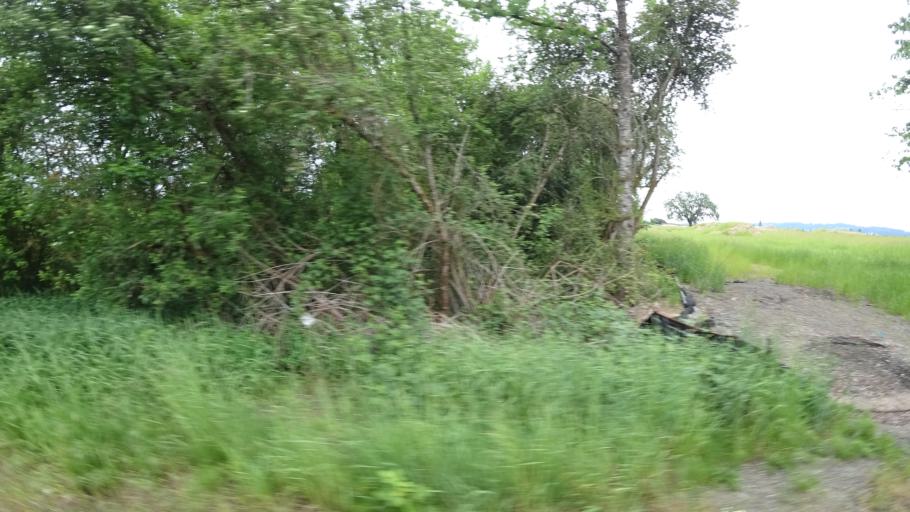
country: US
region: Oregon
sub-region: Washington County
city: Aloha
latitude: 45.4938
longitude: -122.9125
